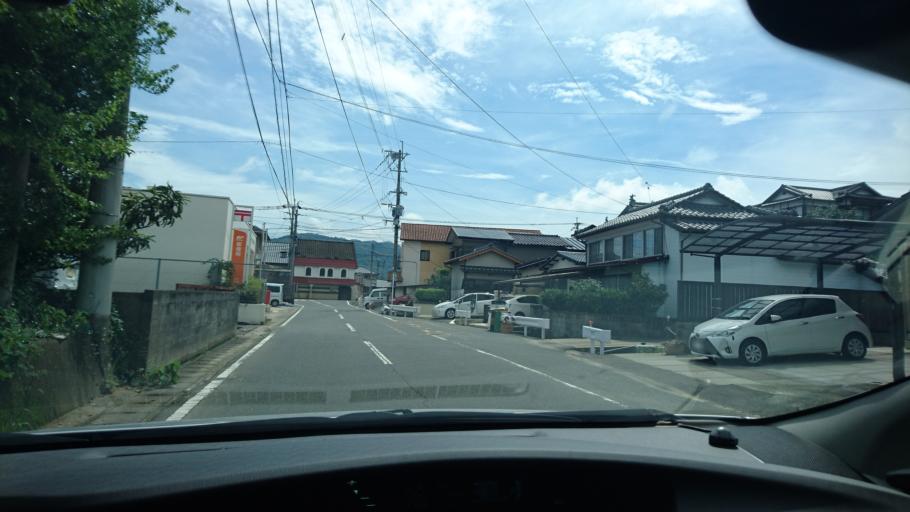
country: JP
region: Saga Prefecture
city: Takeocho-takeo
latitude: 33.2212
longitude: 130.0721
